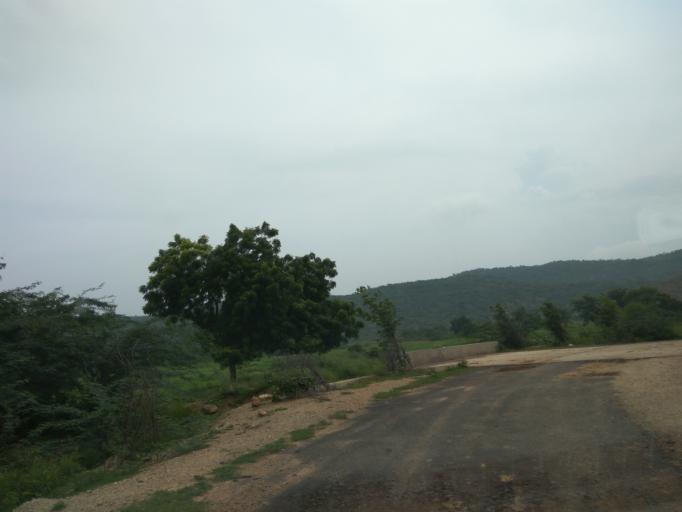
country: IN
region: Andhra Pradesh
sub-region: Prakasam
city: Cumbum
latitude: 15.4505
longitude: 79.0785
